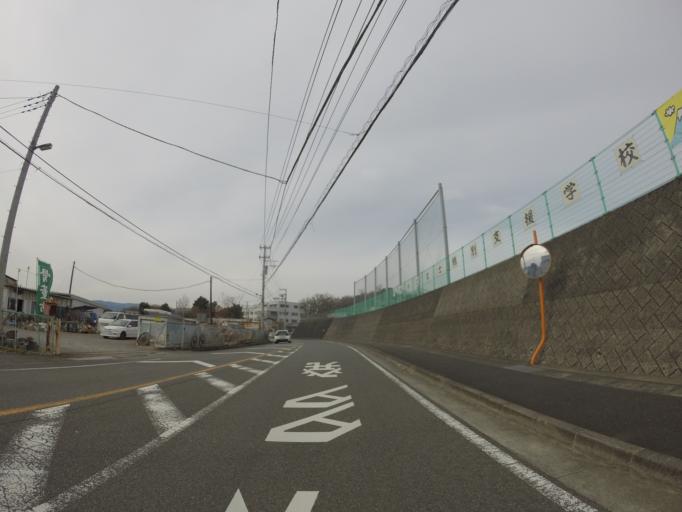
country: JP
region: Shizuoka
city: Fuji
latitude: 35.2148
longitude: 138.6713
